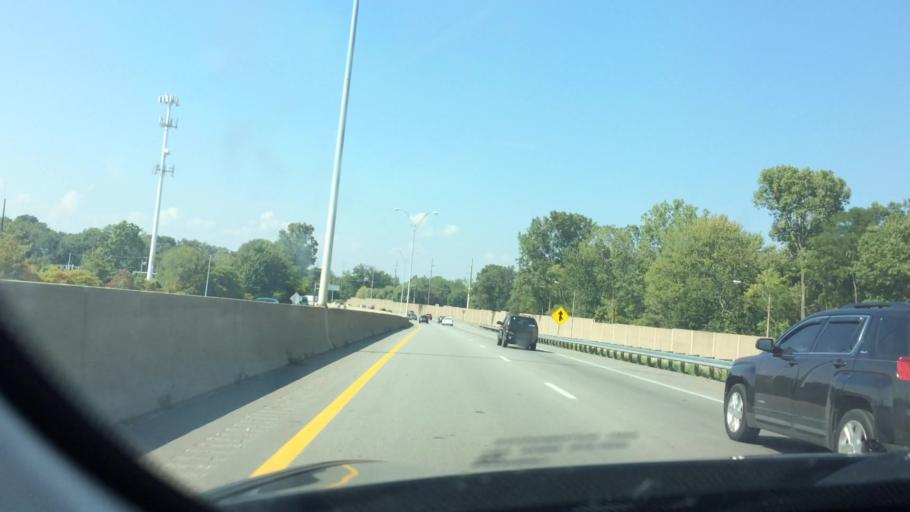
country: US
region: Ohio
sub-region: Lucas County
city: Ottawa Hills
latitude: 41.6872
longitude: -83.6241
